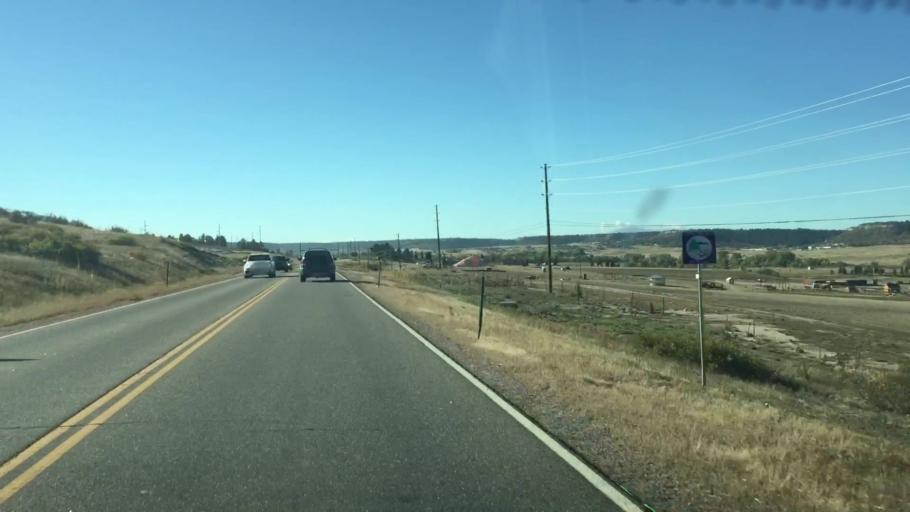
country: US
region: Colorado
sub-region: Douglas County
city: The Pinery
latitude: 39.4226
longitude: -104.7608
